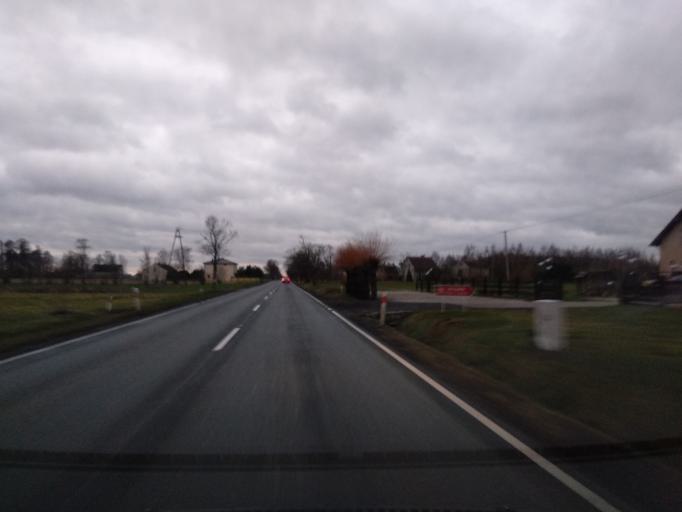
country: PL
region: Greater Poland Voivodeship
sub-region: Powiat koninski
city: Stare Miasto
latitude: 52.1370
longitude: 18.1877
